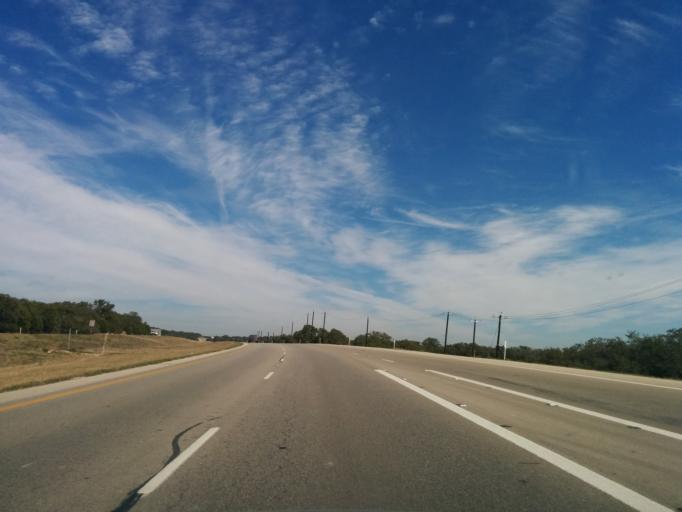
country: US
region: Texas
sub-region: Comal County
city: Bulverde
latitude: 29.7462
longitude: -98.4327
